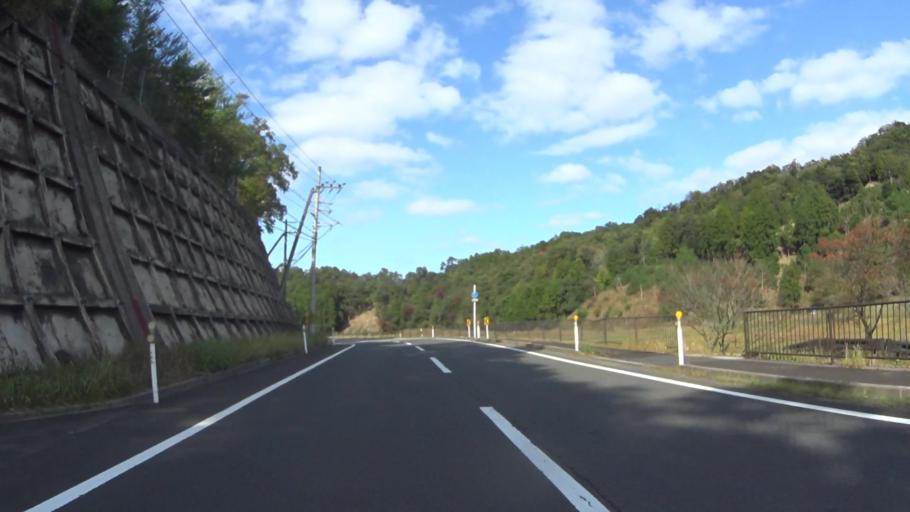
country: JP
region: Hyogo
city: Toyooka
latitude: 35.5630
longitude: 134.9781
